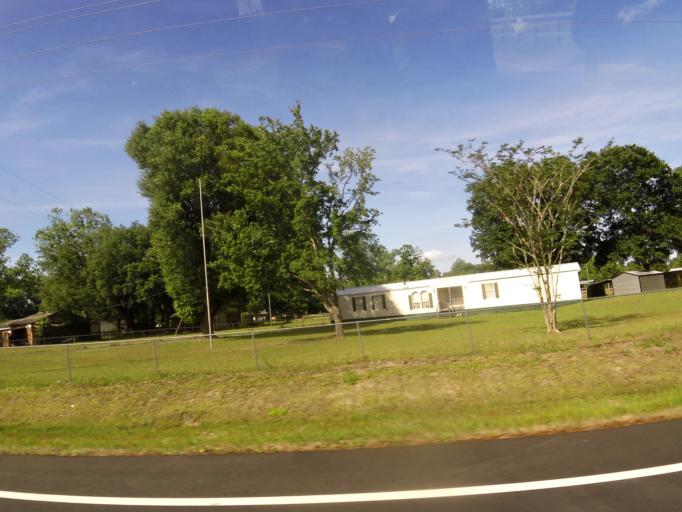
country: US
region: Florida
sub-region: Nassau County
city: Hilliard
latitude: 30.6211
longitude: -81.8861
